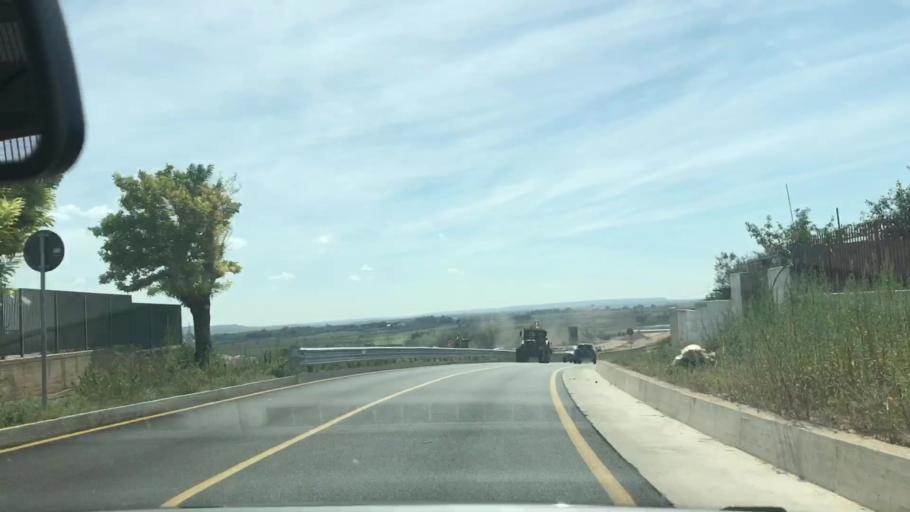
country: IT
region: Apulia
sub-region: Provincia di Bari
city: Altamura
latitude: 40.8106
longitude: 16.5550
